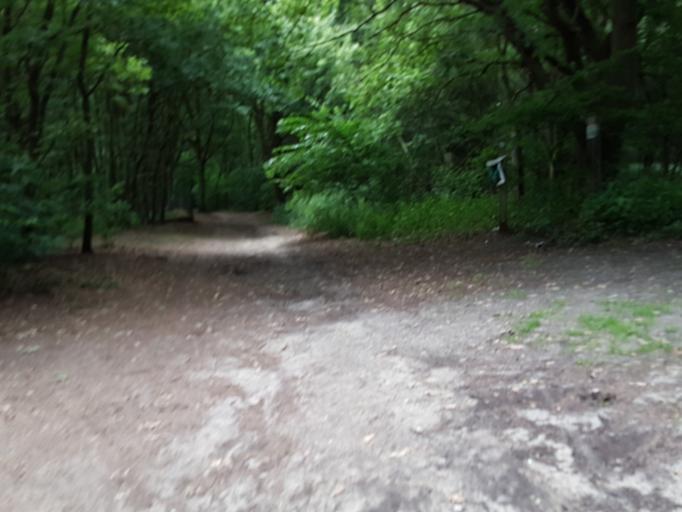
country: BE
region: Flanders
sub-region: Provincie Antwerpen
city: Mechelen
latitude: 51.0488
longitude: 4.4910
